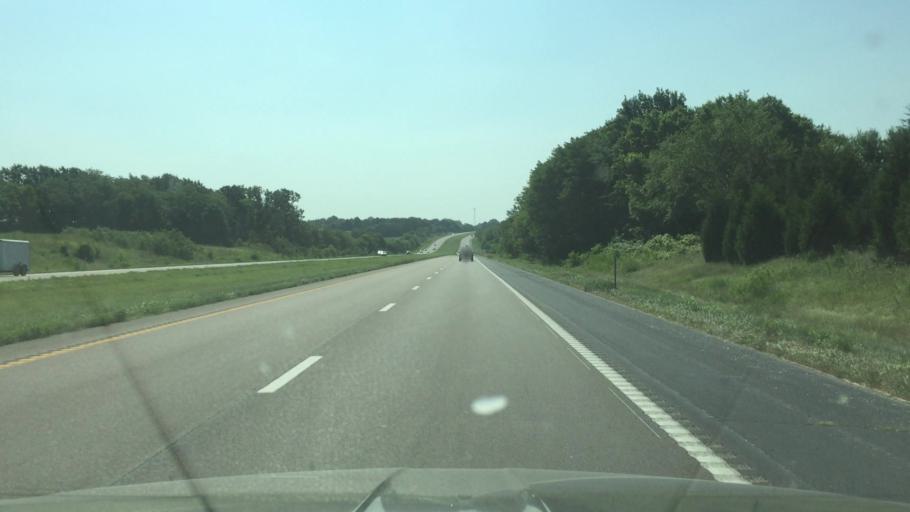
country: US
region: Missouri
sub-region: Pettis County
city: La Monte
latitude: 38.7449
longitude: -93.3341
